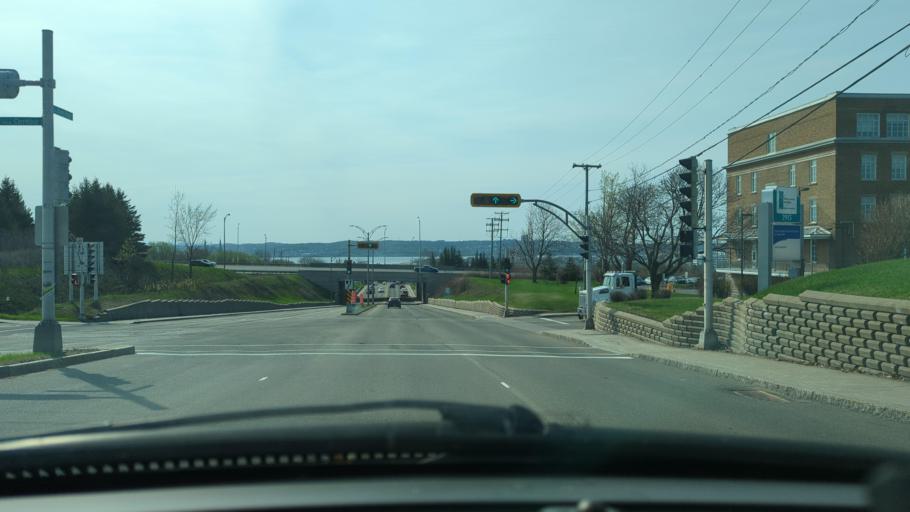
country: CA
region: Quebec
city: Quebec
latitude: 46.8578
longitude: -71.2196
